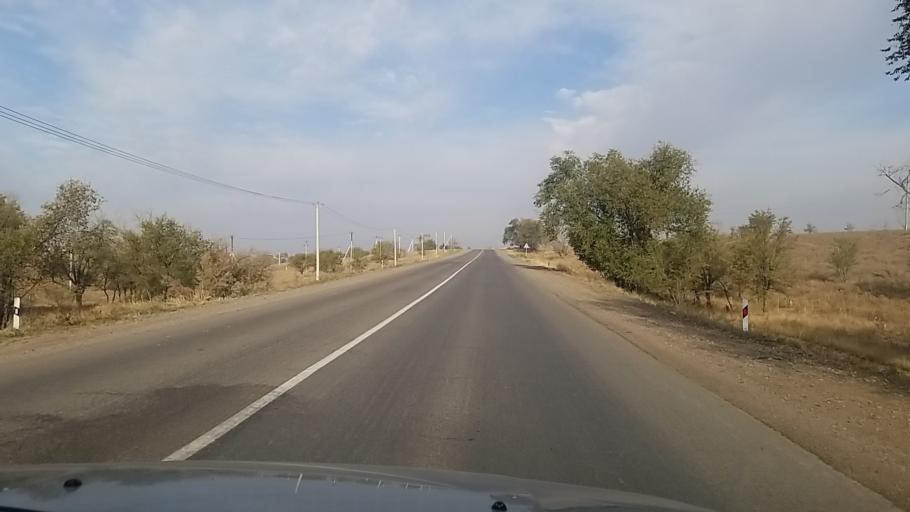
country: KZ
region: Almaty Oblysy
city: Burunday
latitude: 43.4721
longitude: 76.6962
